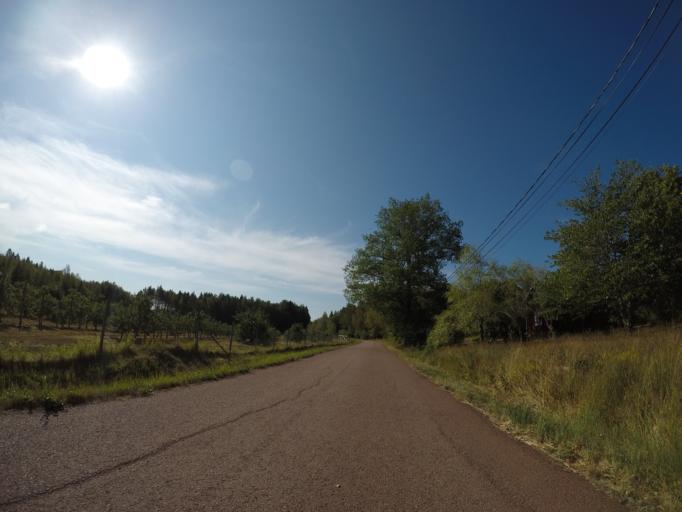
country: AX
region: Alands landsbygd
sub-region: Finstroem
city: Finstroem
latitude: 60.2789
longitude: 19.9172
